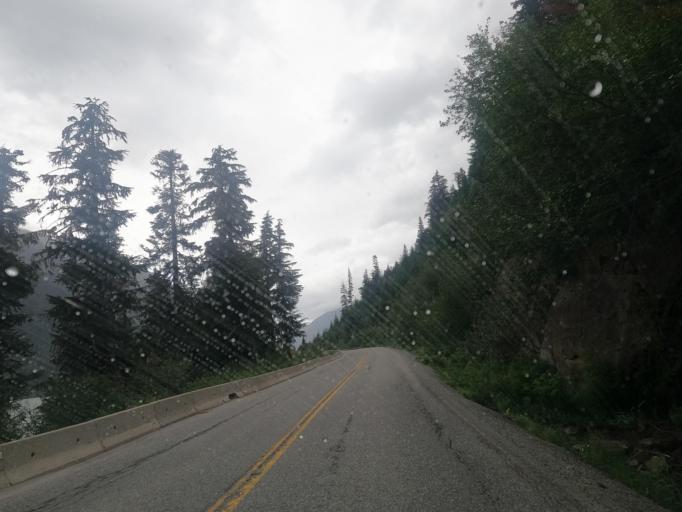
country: CA
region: British Columbia
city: Lillooet
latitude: 50.4019
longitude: -122.3092
